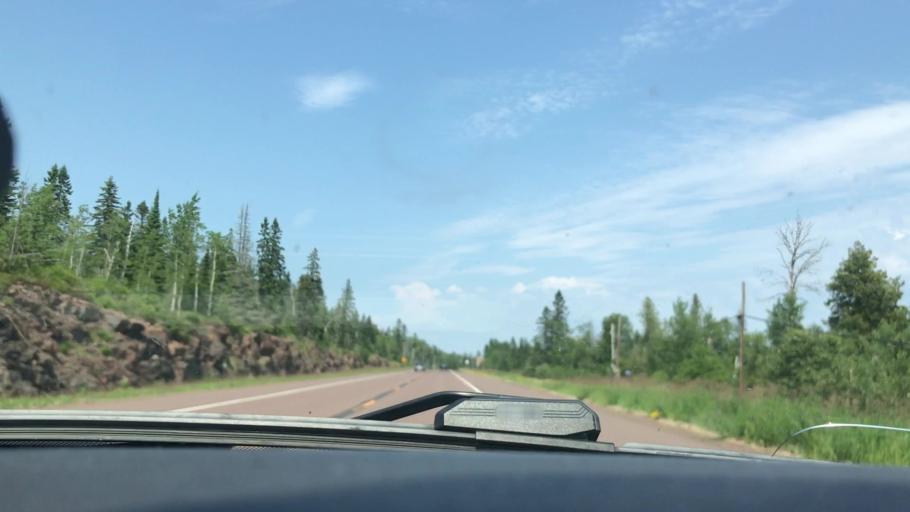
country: US
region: Minnesota
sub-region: Cook County
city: Grand Marais
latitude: 47.6156
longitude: -90.7573
